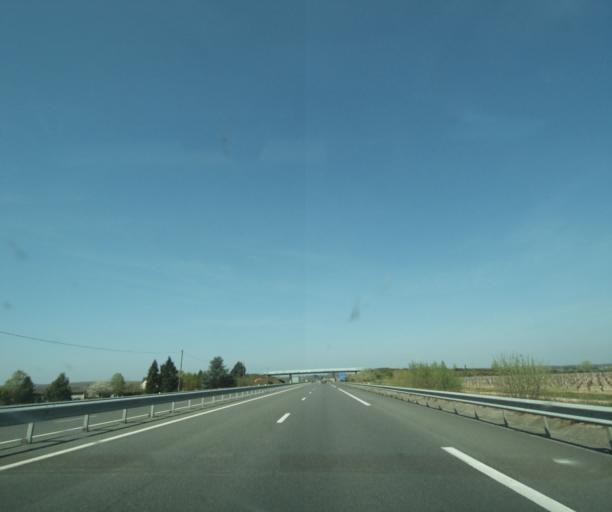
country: FR
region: Bourgogne
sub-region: Departement de la Nievre
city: Pouilly-sur-Loire
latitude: 47.3222
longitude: 2.9349
